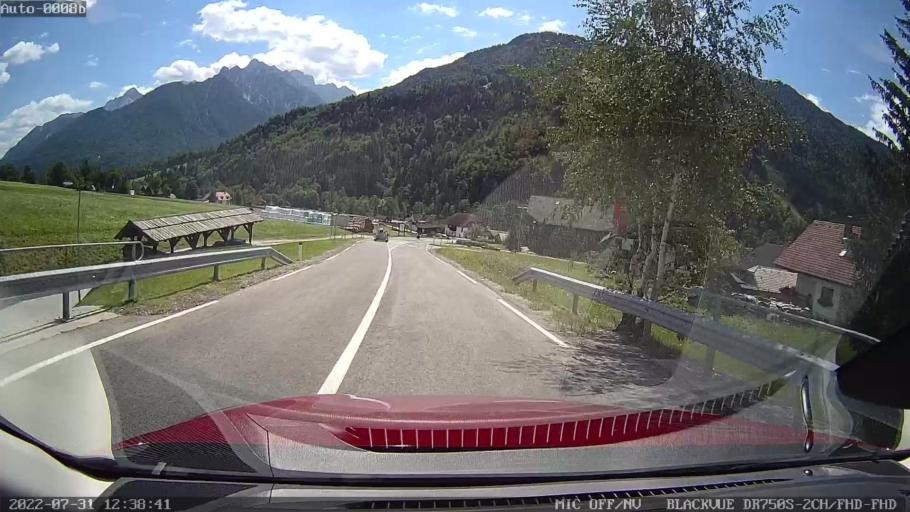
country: SI
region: Kranjska Gora
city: Kranjska Gora
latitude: 46.4943
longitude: 13.7595
